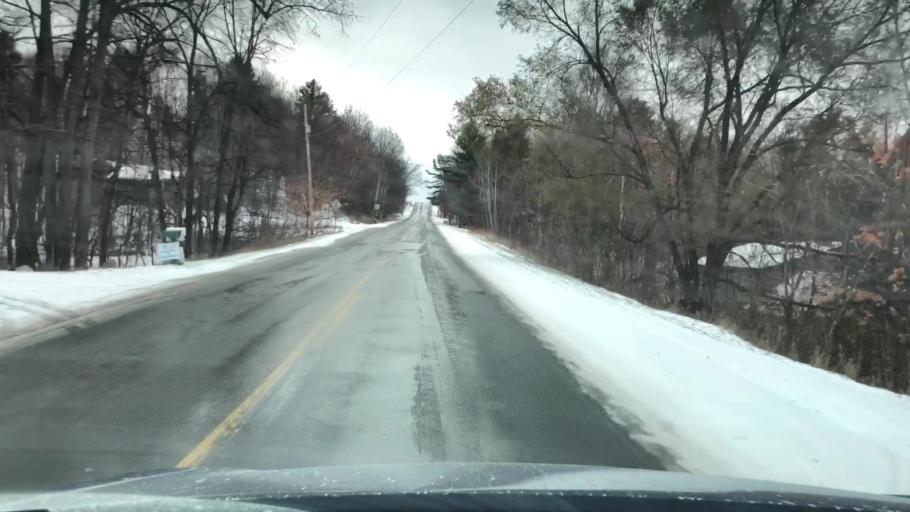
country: US
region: Michigan
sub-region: Antrim County
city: Elk Rapids
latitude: 44.8909
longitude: -85.5154
